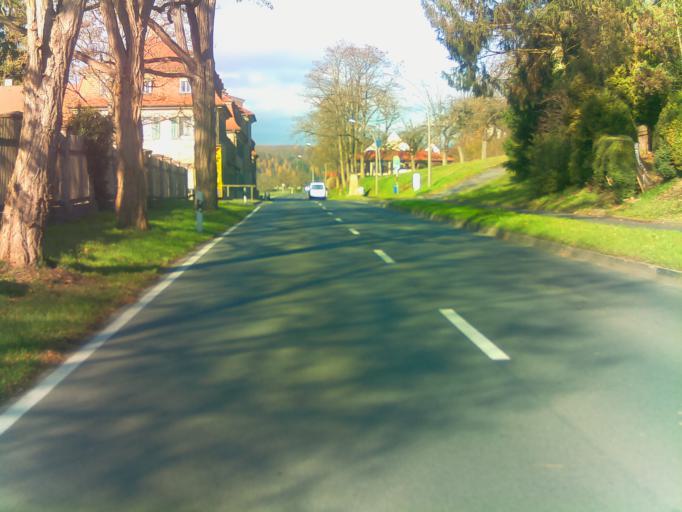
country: DE
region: Bavaria
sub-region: Regierungsbezirk Unterfranken
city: Bad Kissingen
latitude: 50.2206
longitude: 10.0700
